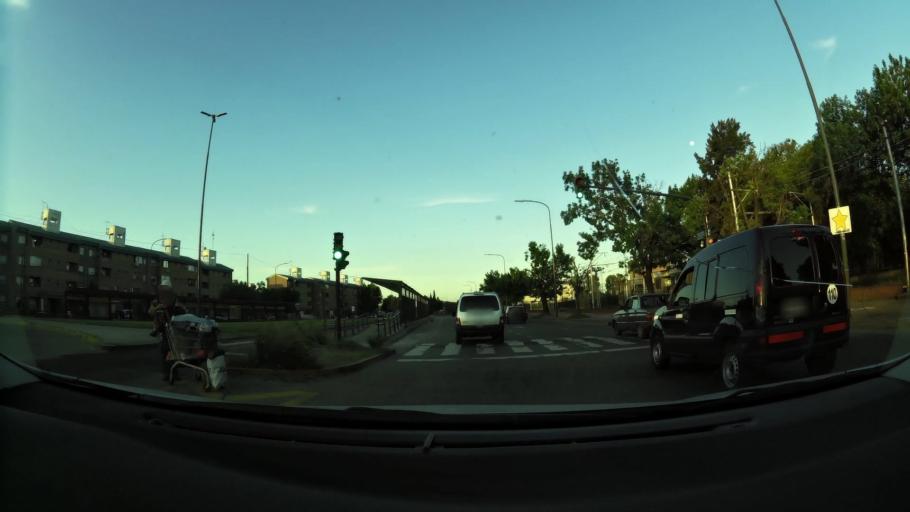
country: AR
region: Buenos Aires F.D.
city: Villa Lugano
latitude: -34.6795
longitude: -58.4658
